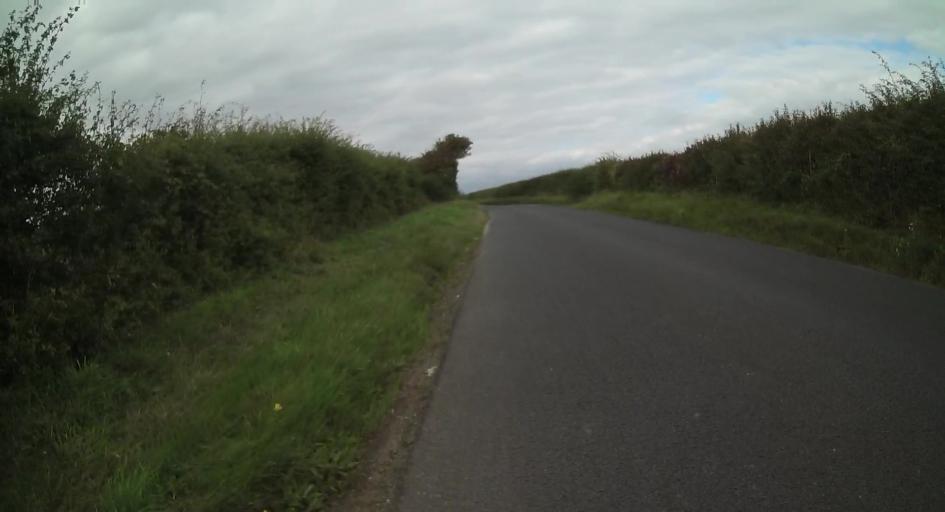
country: GB
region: England
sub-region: Isle of Wight
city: Yarmouth
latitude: 50.6953
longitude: -1.4830
